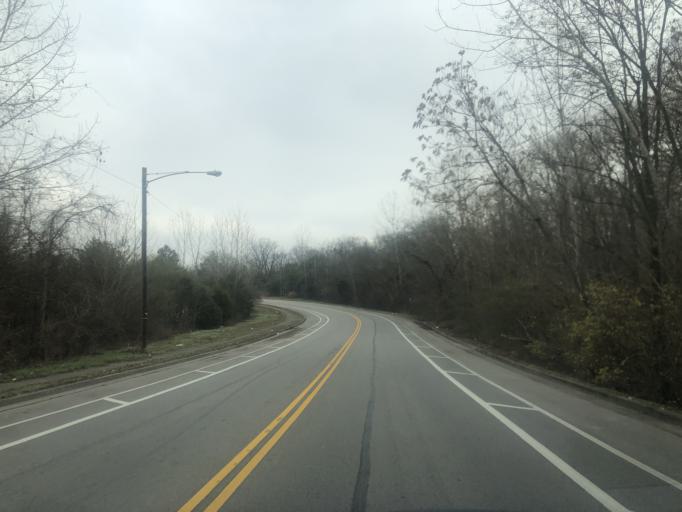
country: US
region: Tennessee
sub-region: Rutherford County
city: La Vergne
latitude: 36.0710
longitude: -86.6474
